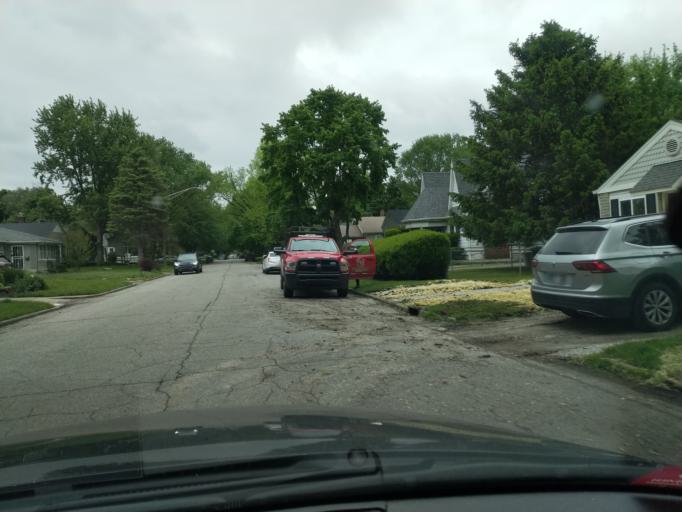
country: US
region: Indiana
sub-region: Marion County
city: Broad Ripple
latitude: 39.8440
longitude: -86.1278
